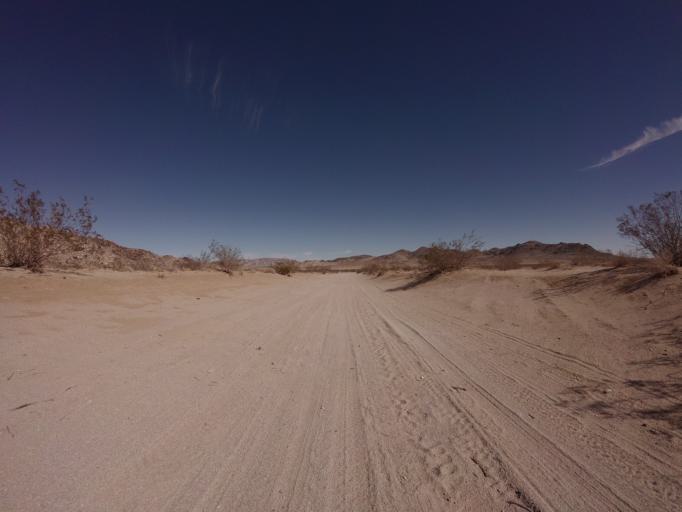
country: US
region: California
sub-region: San Bernardino County
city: Joshua Tree
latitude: 34.3206
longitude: -116.3916
